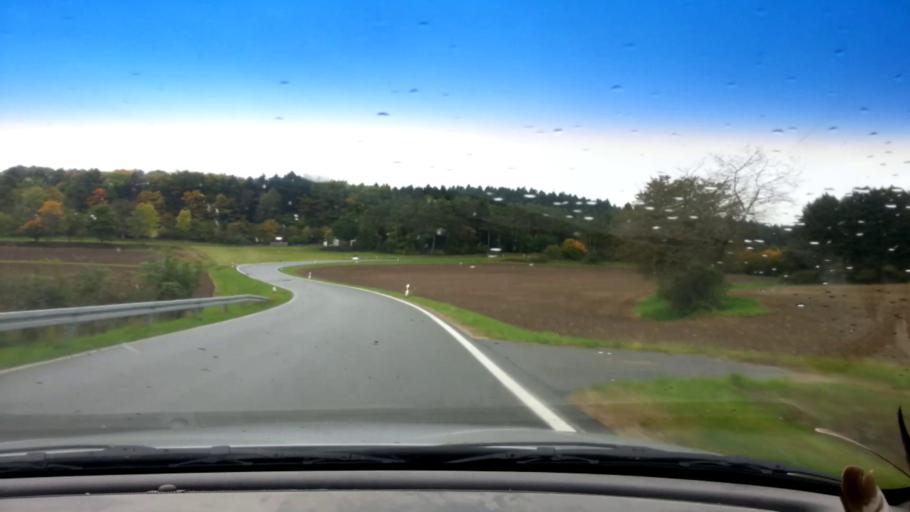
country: DE
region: Bavaria
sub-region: Upper Franconia
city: Poxdorf
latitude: 49.8783
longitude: 11.1024
